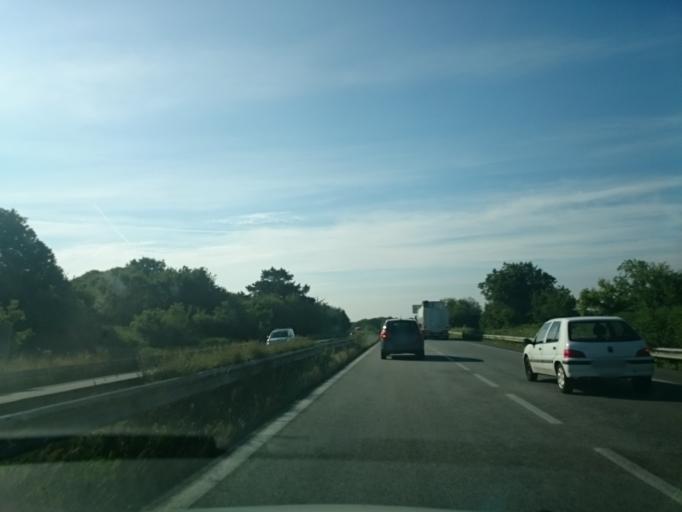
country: FR
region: Brittany
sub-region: Departement du Finistere
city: Saint-Yvi
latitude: 47.9279
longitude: -3.8996
